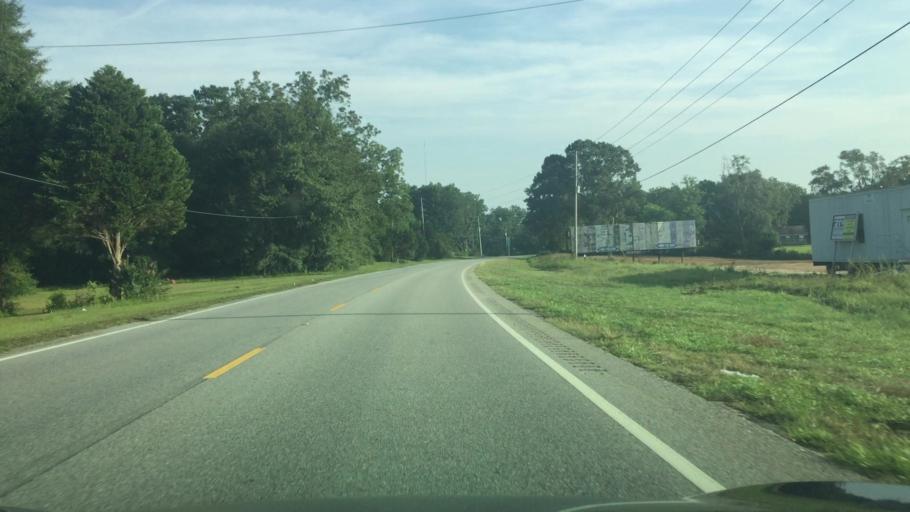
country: US
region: Alabama
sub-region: Covington County
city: Andalusia
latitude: 31.2692
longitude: -86.4739
